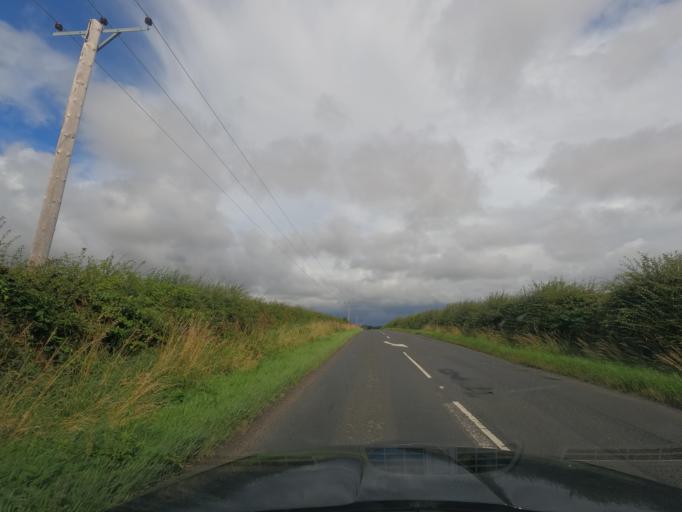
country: GB
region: England
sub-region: Northumberland
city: Ancroft
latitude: 55.6734
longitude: -2.0012
